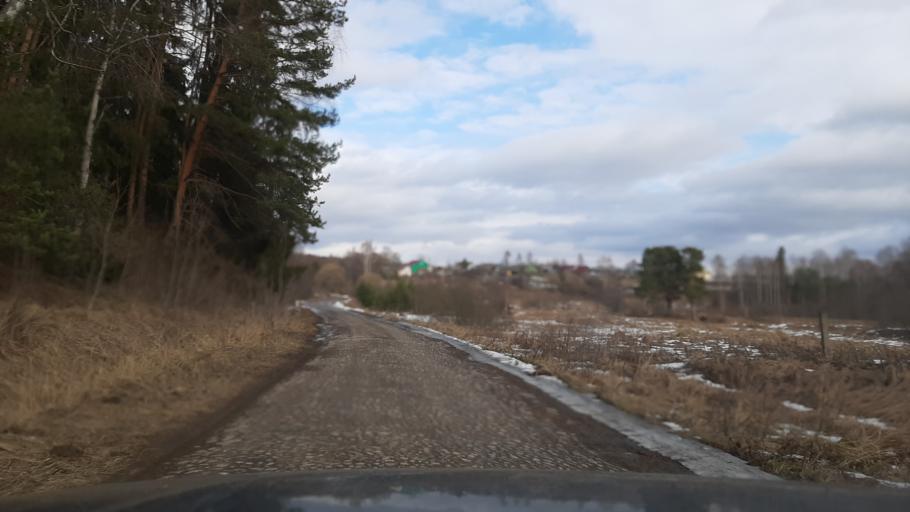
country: RU
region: Ivanovo
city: Teykovo
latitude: 56.8967
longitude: 40.6726
